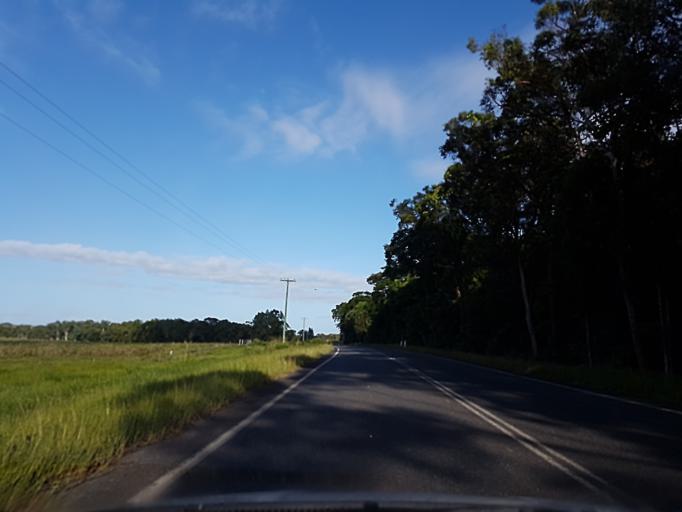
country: AU
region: Queensland
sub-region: Cairns
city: Port Douglas
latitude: -16.3190
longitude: 145.4048
